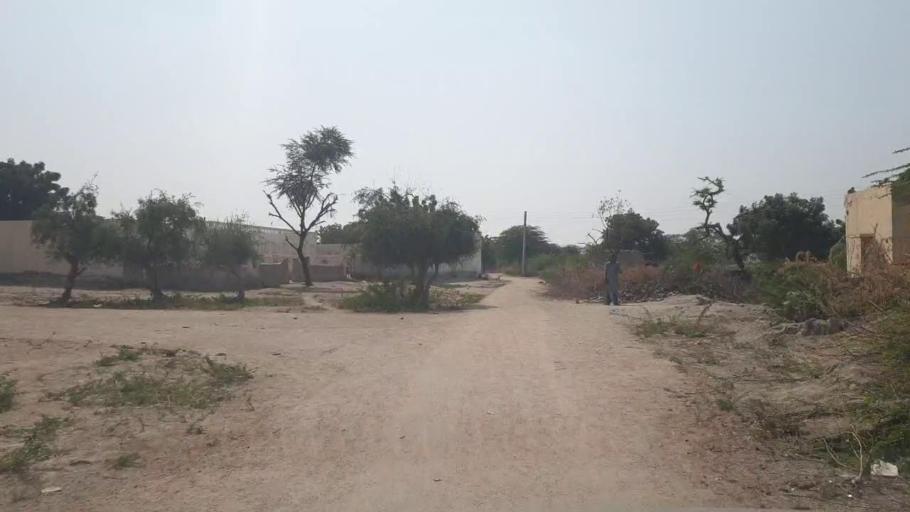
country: PK
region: Sindh
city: Chor
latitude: 25.4751
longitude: 69.7750
